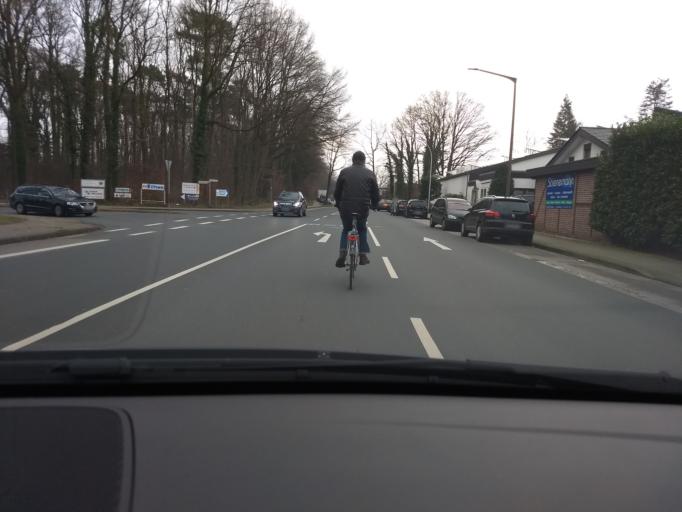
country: DE
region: North Rhine-Westphalia
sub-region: Regierungsbezirk Munster
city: Borken
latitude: 51.8505
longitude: 6.8697
